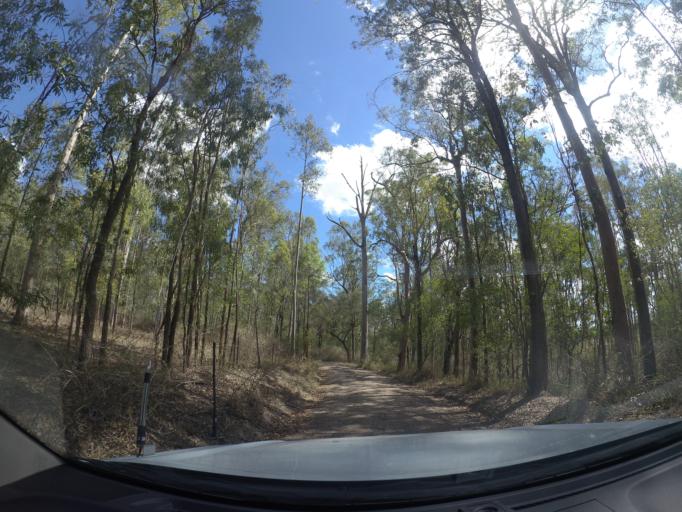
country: AU
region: Queensland
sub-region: Logan
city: Cedar Vale
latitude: -27.8390
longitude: 152.9748
